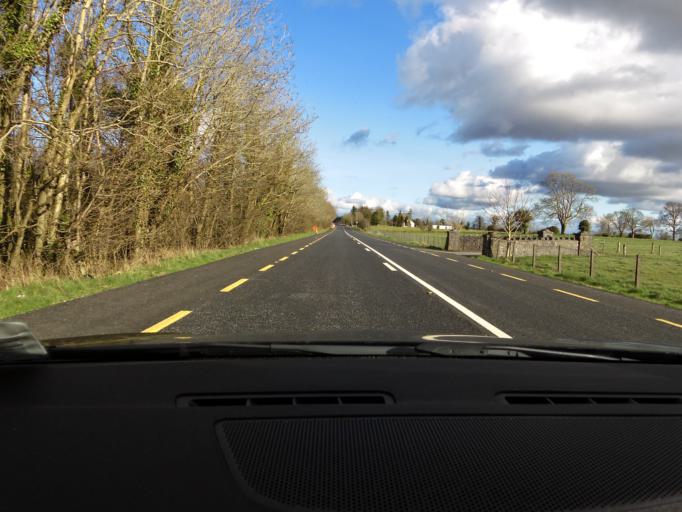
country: IE
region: Connaught
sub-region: Roscommon
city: Castlerea
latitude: 53.6970
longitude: -8.4483
